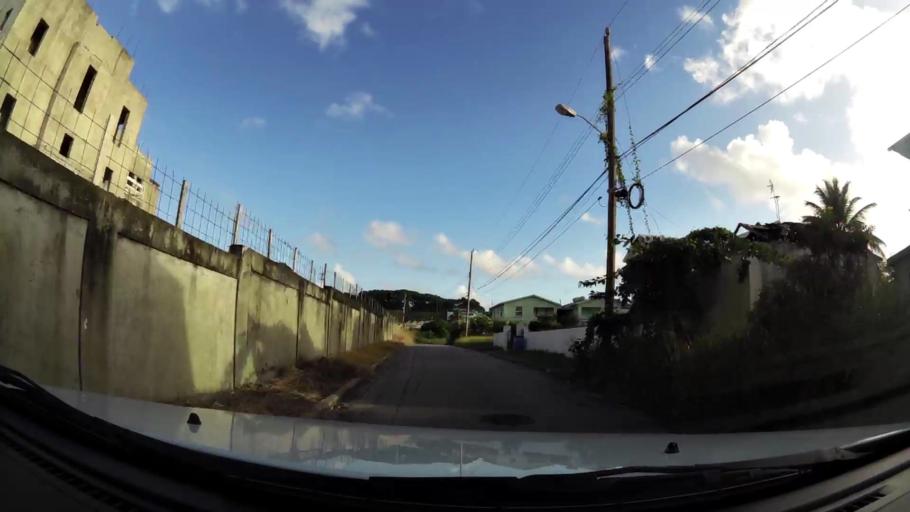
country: BB
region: Christ Church
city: Oistins
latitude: 13.0668
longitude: -59.5531
